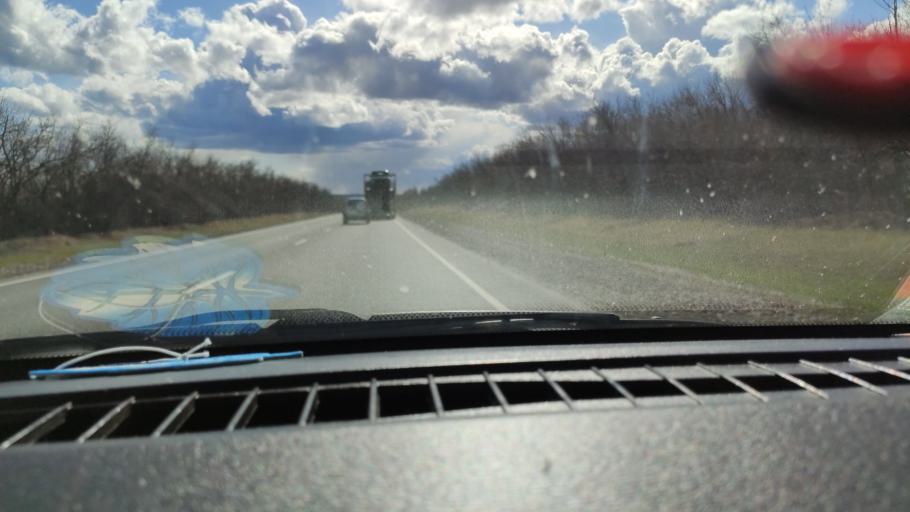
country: RU
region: Saratov
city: Khvalynsk
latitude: 52.5923
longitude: 48.1326
